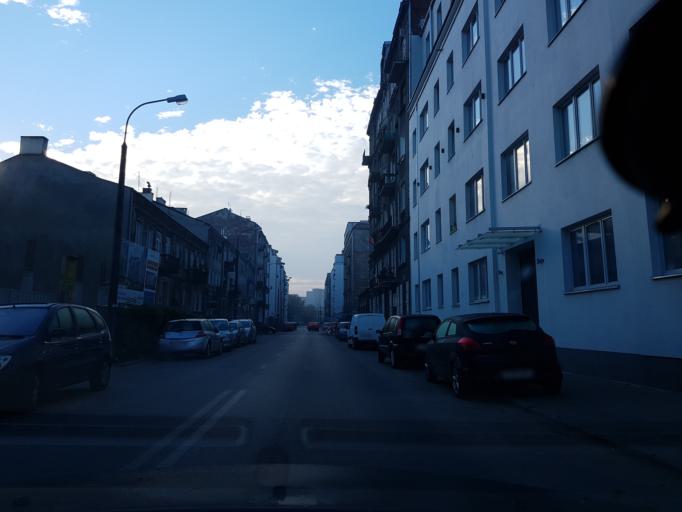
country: PL
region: Masovian Voivodeship
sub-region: Warszawa
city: Praga Polnoc
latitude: 52.2611
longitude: 21.0396
